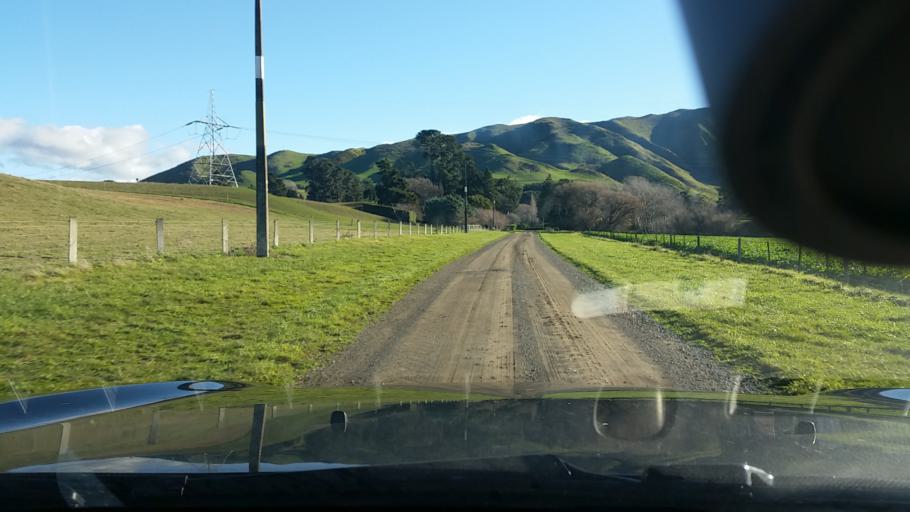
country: NZ
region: Marlborough
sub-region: Marlborough District
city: Blenheim
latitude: -41.6385
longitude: 174.0267
